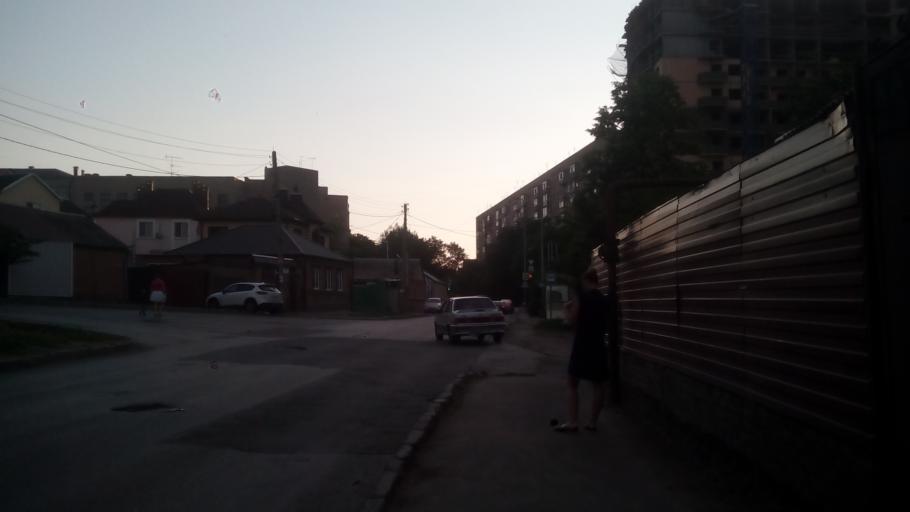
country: RU
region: Rostov
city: Imeni Chkalova
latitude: 47.2566
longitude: 39.7745
